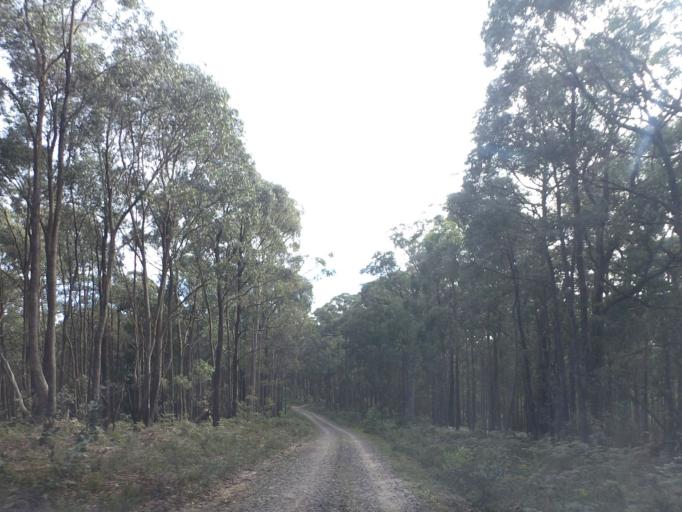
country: AU
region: Victoria
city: Brown Hill
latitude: -37.4894
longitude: 144.1954
